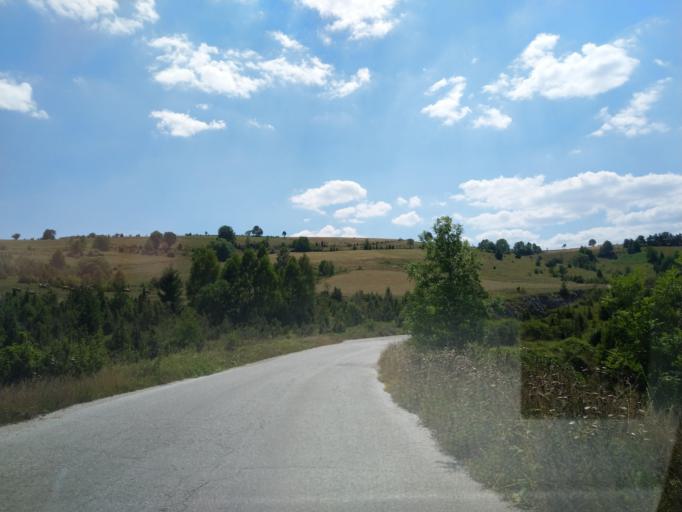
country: RS
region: Central Serbia
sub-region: Zlatiborski Okrug
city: Nova Varos
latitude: 43.4365
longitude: 19.9595
